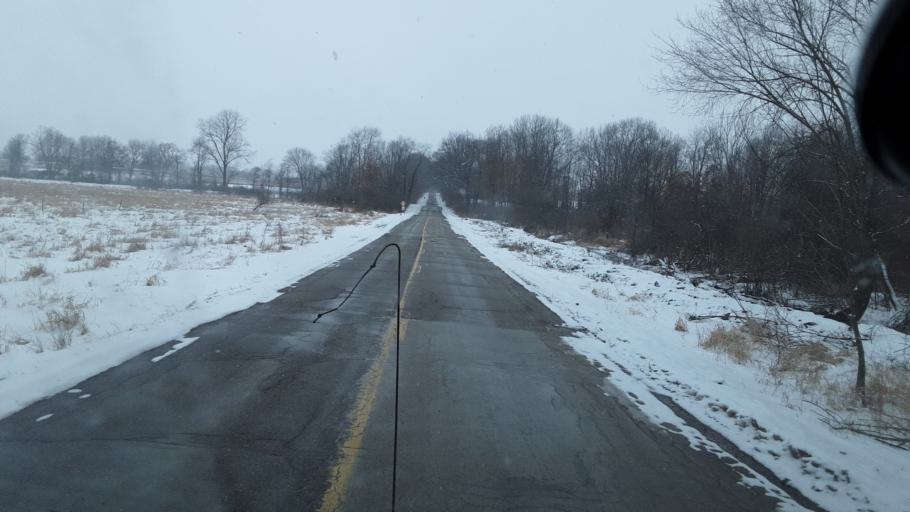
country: US
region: Michigan
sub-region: Ingham County
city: Leslie
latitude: 42.4911
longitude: -84.3672
